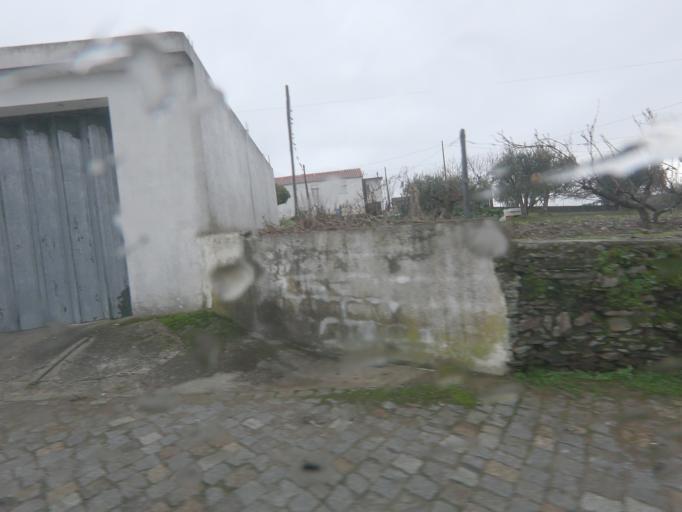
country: PT
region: Vila Real
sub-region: Peso da Regua
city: Peso da Regua
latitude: 41.1814
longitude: -7.7180
